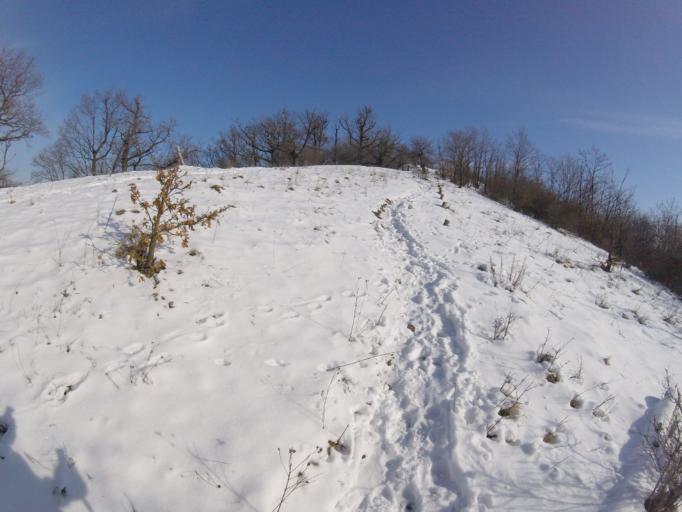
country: HU
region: Heves
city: Recsk
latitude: 47.8843
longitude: 20.0816
